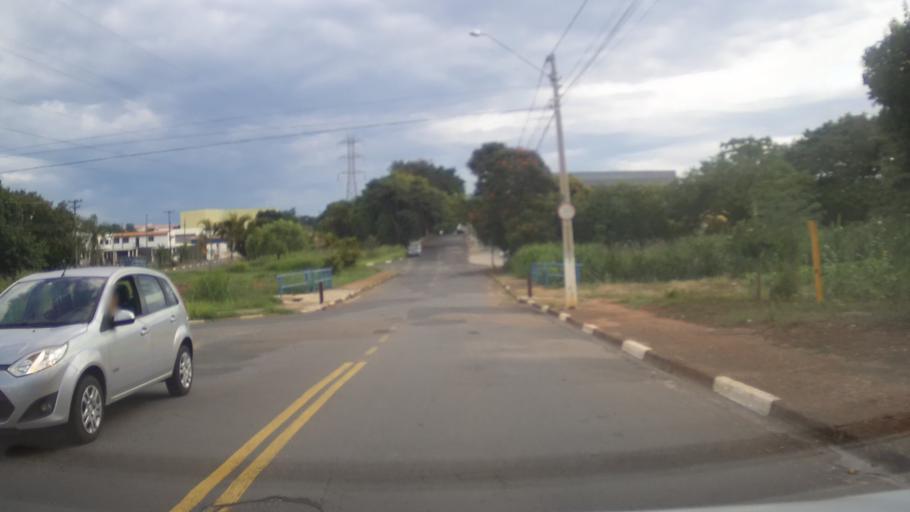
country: BR
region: Sao Paulo
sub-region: Campinas
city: Campinas
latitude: -22.8807
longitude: -47.1252
